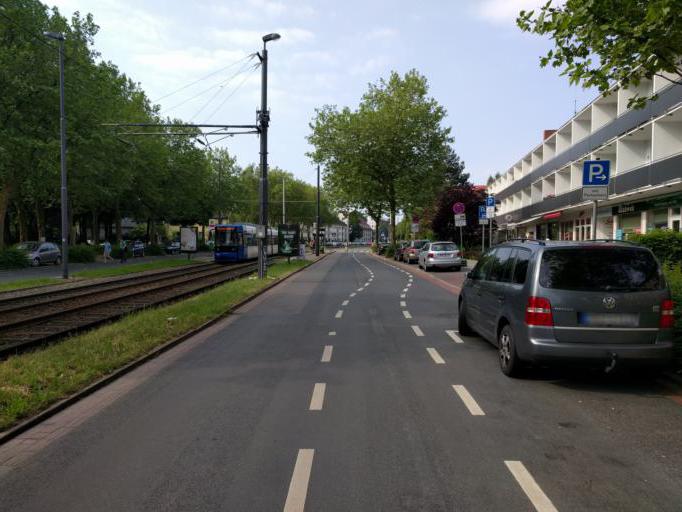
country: DE
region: Bremen
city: Bremen
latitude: 53.0920
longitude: 8.8460
